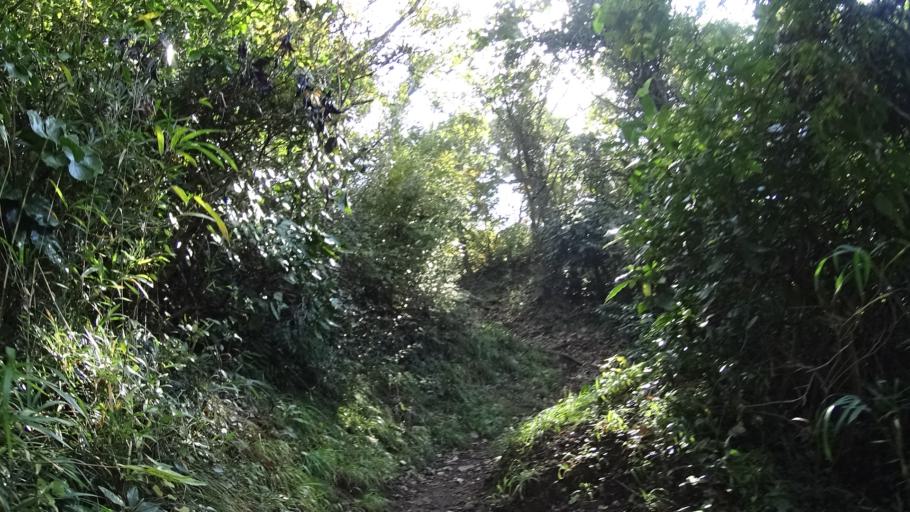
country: JP
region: Kanagawa
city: Hayama
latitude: 35.2818
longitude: 139.6211
